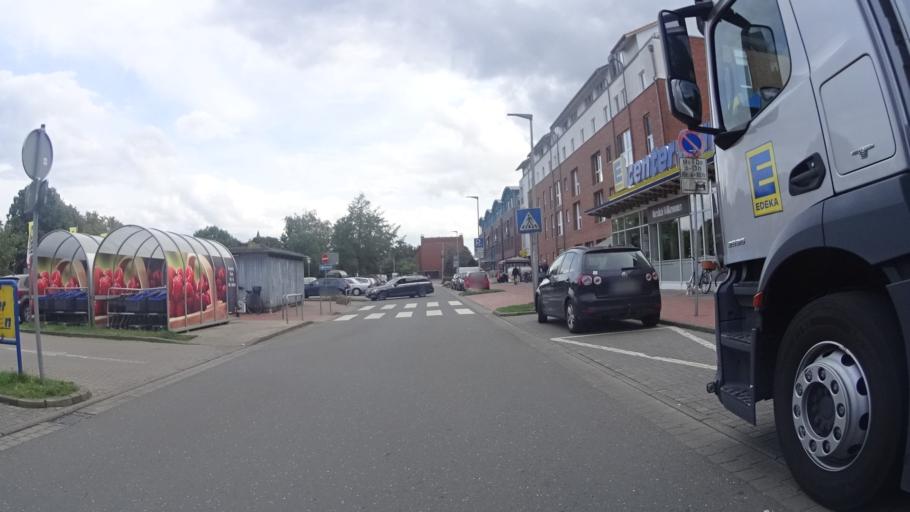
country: DE
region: Schleswig-Holstein
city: Blomesche Wildnis
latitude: 53.7928
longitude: 9.4184
